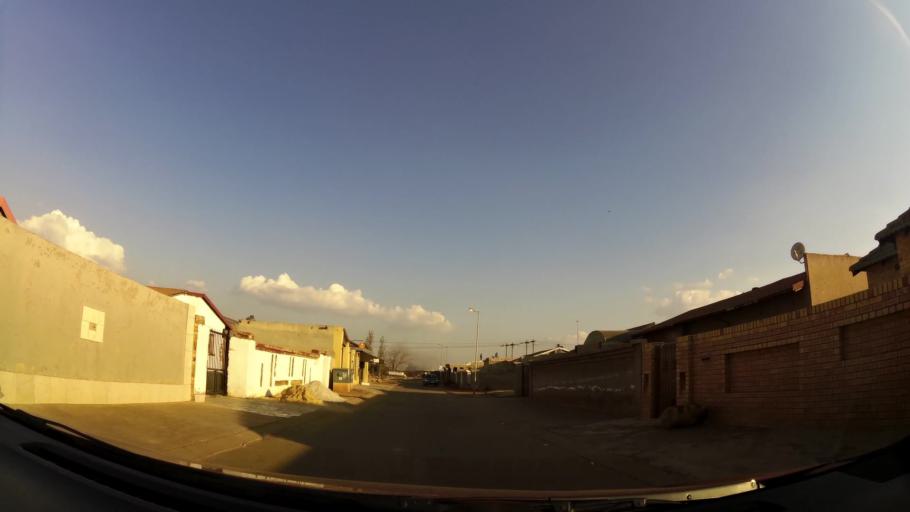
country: ZA
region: Gauteng
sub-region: City of Johannesburg Metropolitan Municipality
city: Soweto
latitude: -26.2325
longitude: 27.8421
